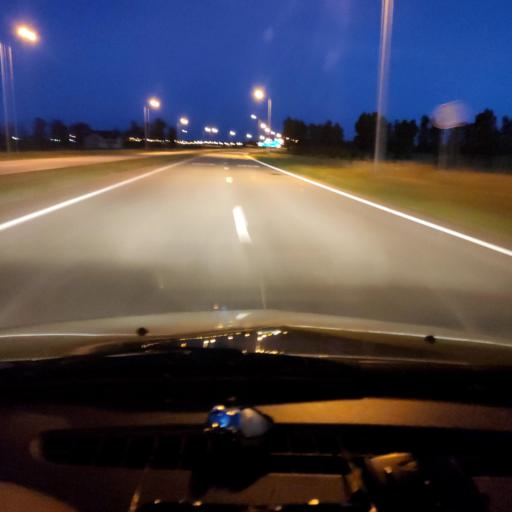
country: RU
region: Belgorod
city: Skorodnoye
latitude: 51.0816
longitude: 37.2125
